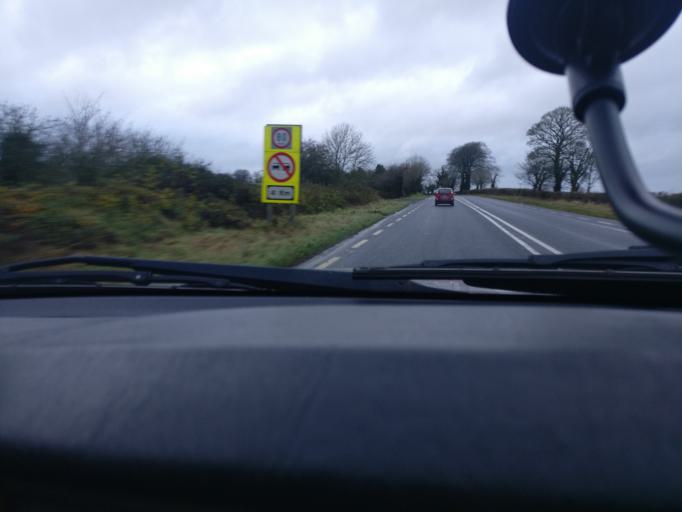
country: IE
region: Leinster
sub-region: Kildare
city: Kilcock
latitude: 53.4212
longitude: -6.7418
